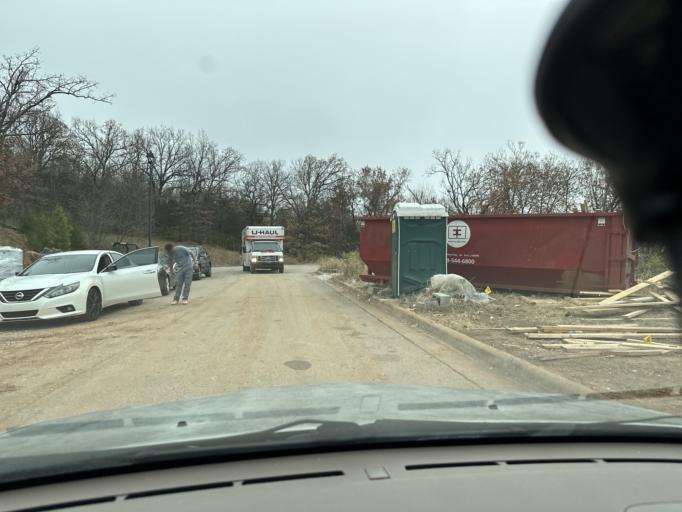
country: US
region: Arkansas
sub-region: Washington County
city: Fayetteville
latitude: 36.0922
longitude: -94.1514
